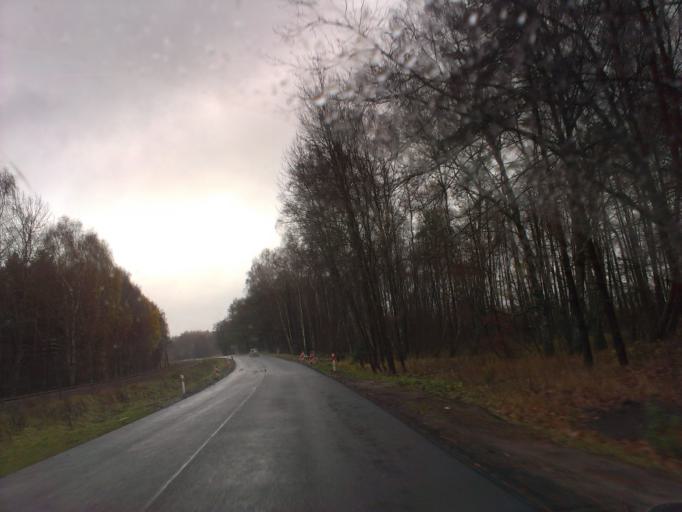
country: PL
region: West Pomeranian Voivodeship
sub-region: Powiat szczecinecki
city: Lubowo
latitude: 53.6060
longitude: 16.4423
